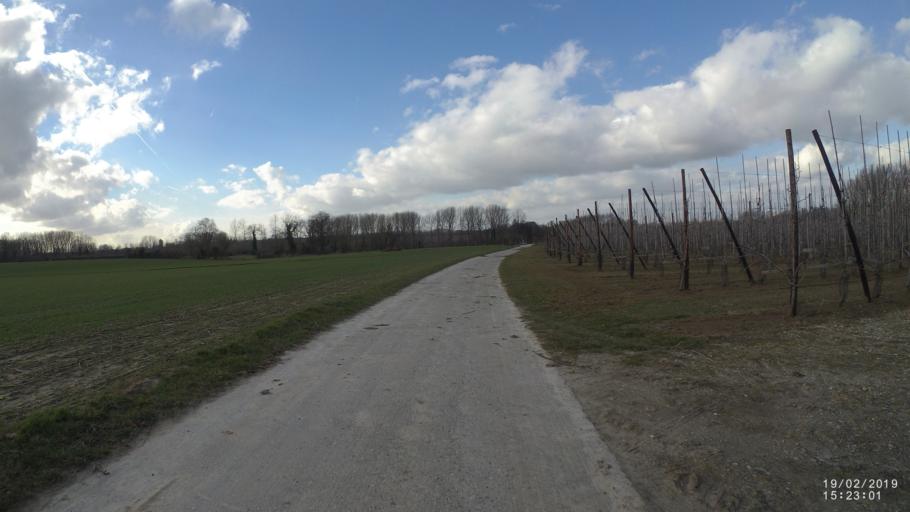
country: BE
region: Flanders
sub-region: Provincie Limburg
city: Tongeren
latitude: 50.7953
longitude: 5.4125
